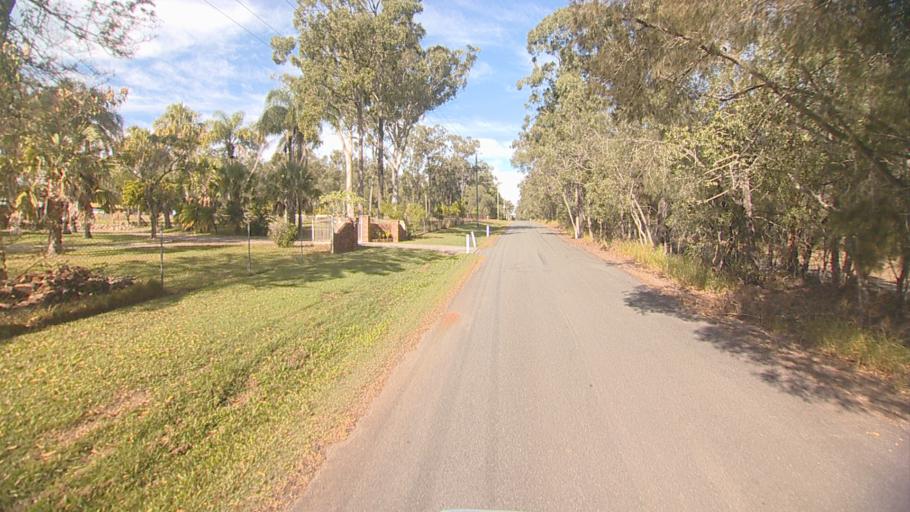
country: AU
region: Queensland
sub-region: Brisbane
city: Forest Lake
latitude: -27.6517
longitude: 152.9835
